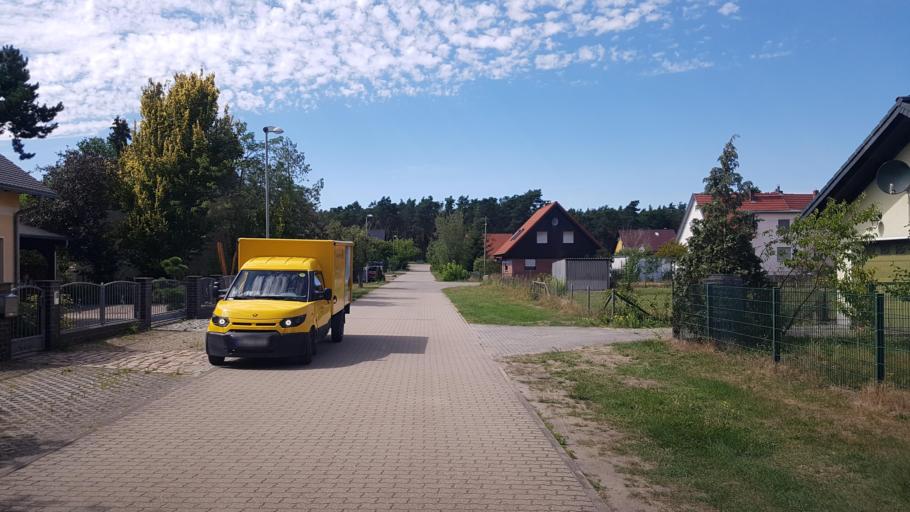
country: DE
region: Brandenburg
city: Luckenwalde
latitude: 52.1127
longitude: 13.1861
